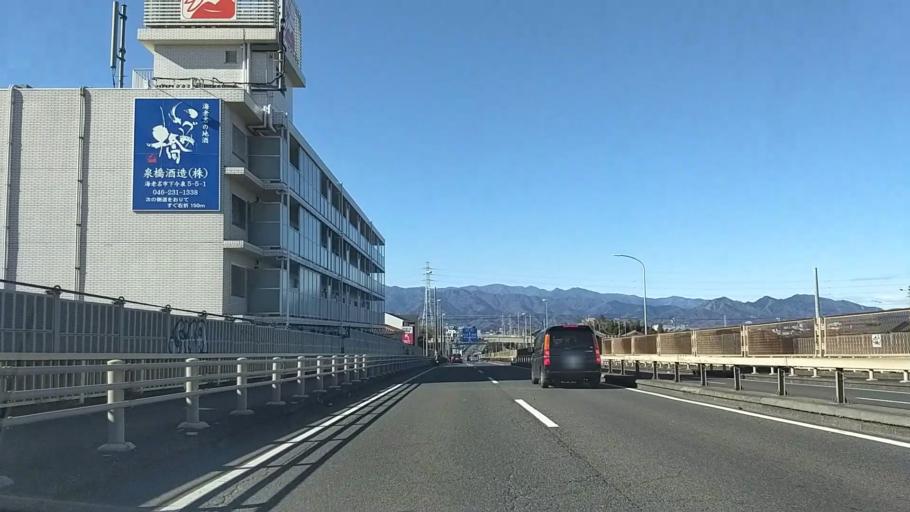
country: JP
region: Kanagawa
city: Zama
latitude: 35.4636
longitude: 139.3980
